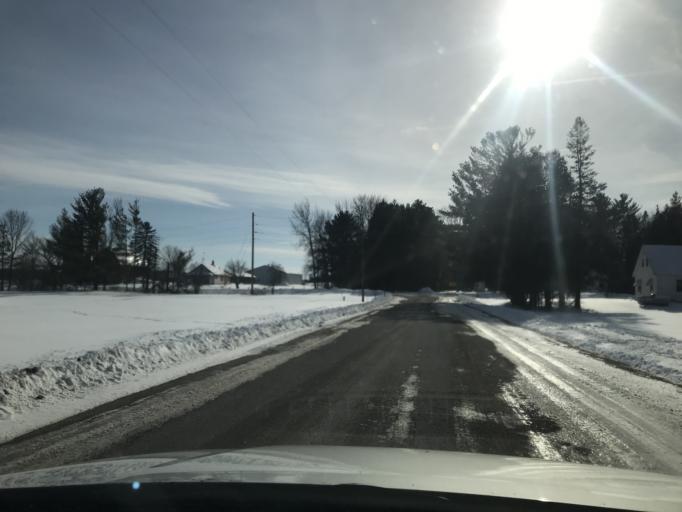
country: US
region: Wisconsin
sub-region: Oconto County
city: Gillett
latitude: 45.1137
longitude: -88.2402
